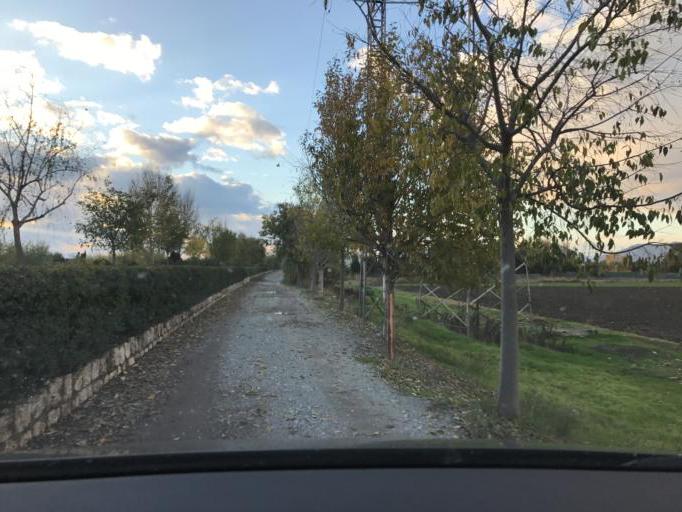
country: ES
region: Andalusia
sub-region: Provincia de Granada
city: Armilla
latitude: 37.1617
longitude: -3.6214
